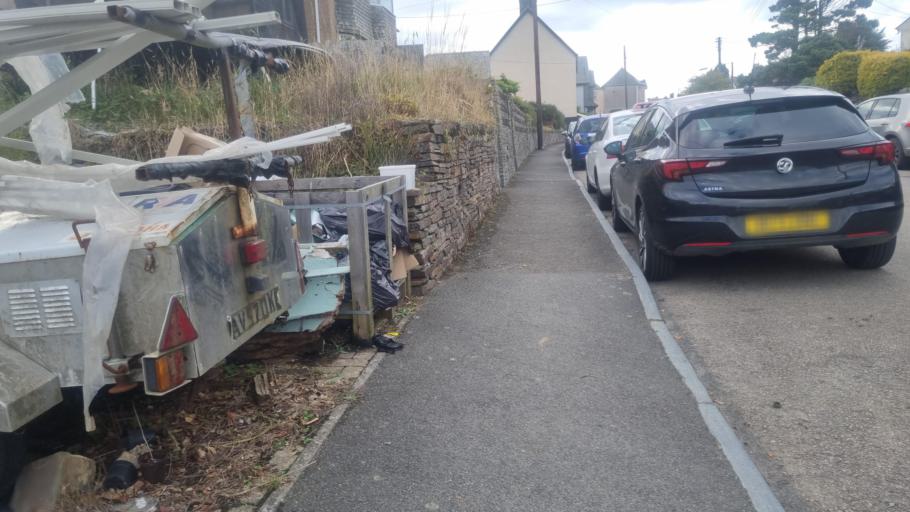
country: GB
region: England
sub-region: Cornwall
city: Tintagel
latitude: 50.6215
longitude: -4.7290
